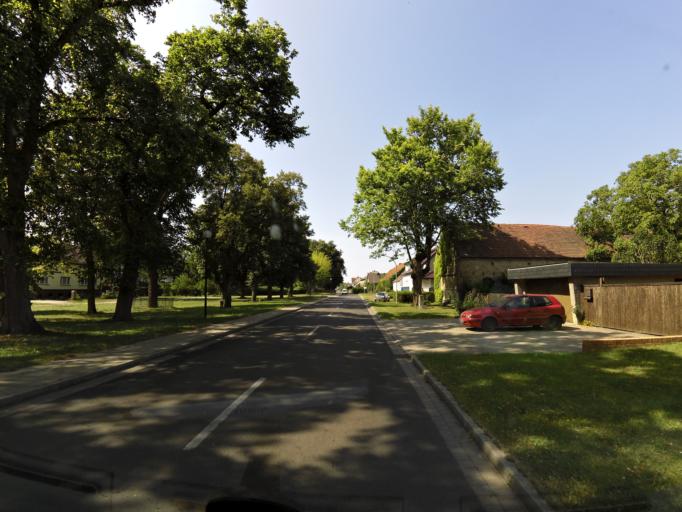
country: DE
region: Brandenburg
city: Zehdenick
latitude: 53.0091
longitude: 13.2918
